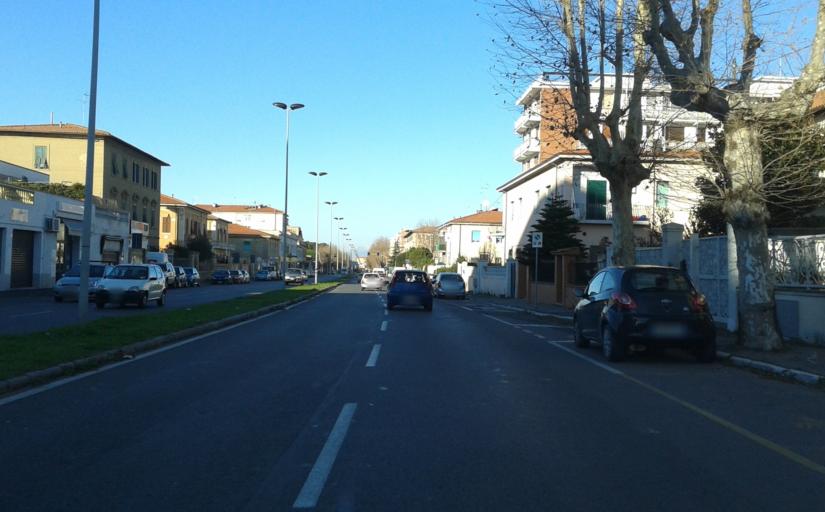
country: IT
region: Tuscany
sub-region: Provincia di Livorno
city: Livorno
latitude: 43.5462
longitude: 10.3279
